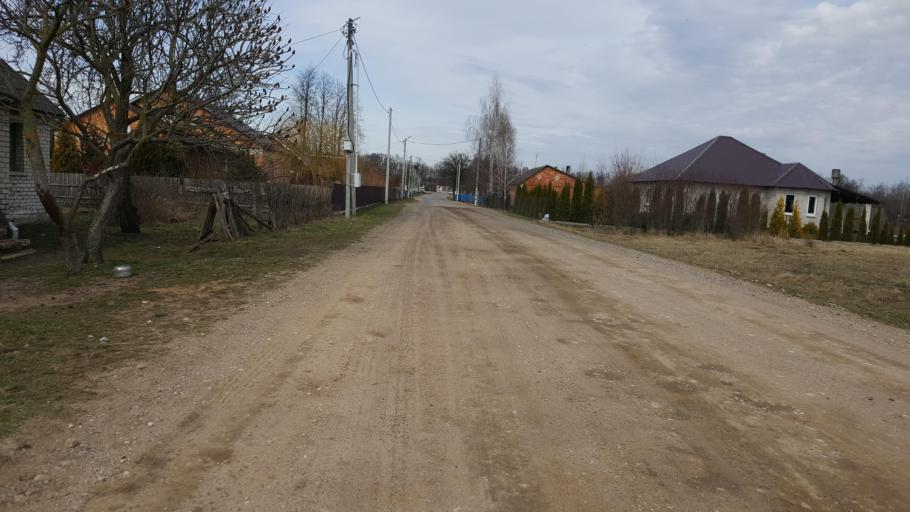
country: BY
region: Brest
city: Kamyanyets
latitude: 52.3905
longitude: 24.0003
